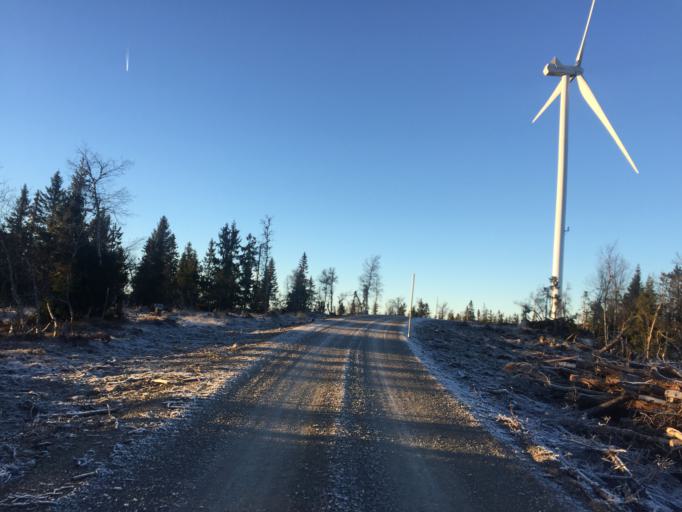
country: NO
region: Hedmark
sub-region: Elverum
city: Elverum
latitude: 61.2121
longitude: 11.7813
